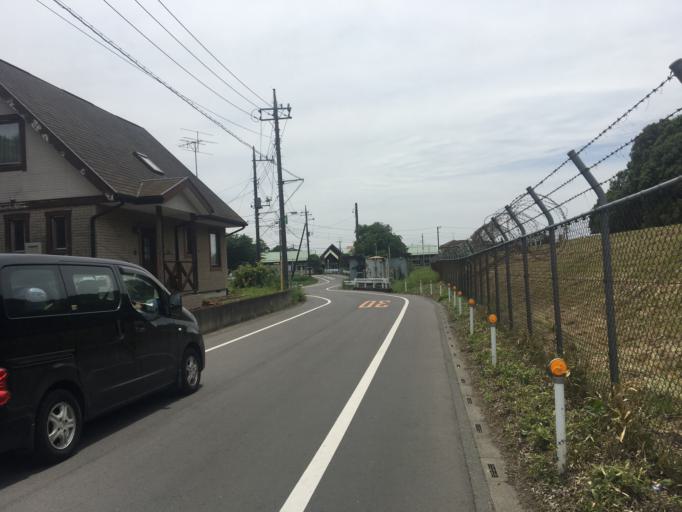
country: JP
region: Saitama
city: Sayama
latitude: 35.8350
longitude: 139.4171
